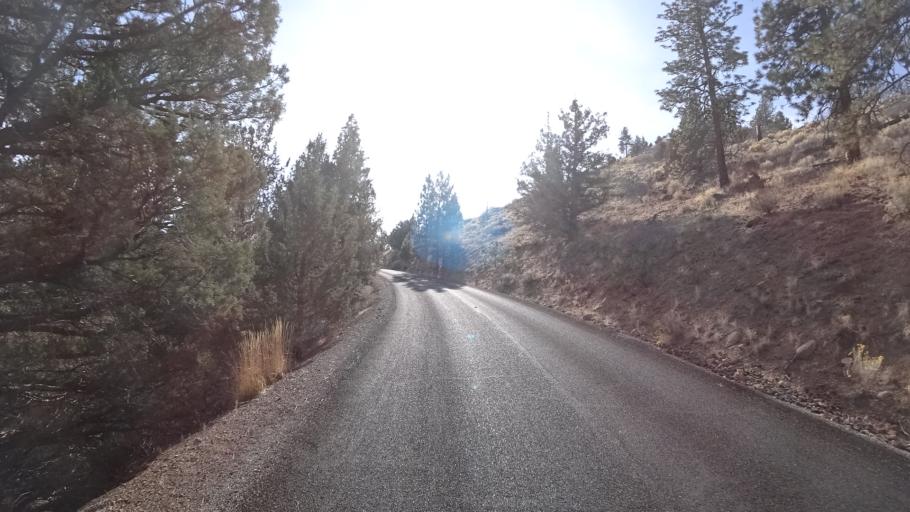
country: US
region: California
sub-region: Siskiyou County
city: Weed
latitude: 41.5032
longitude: -122.3904
